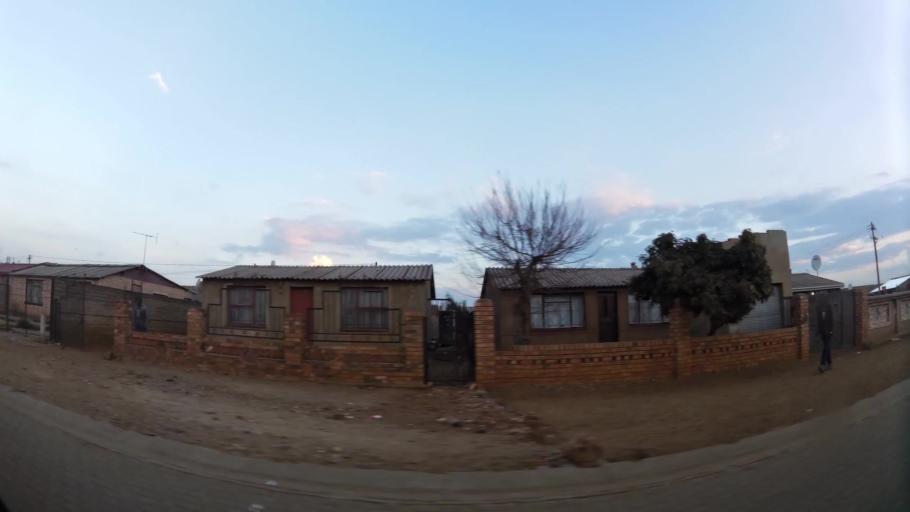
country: ZA
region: Gauteng
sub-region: City of Johannesburg Metropolitan Municipality
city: Orange Farm
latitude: -26.5527
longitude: 27.8739
